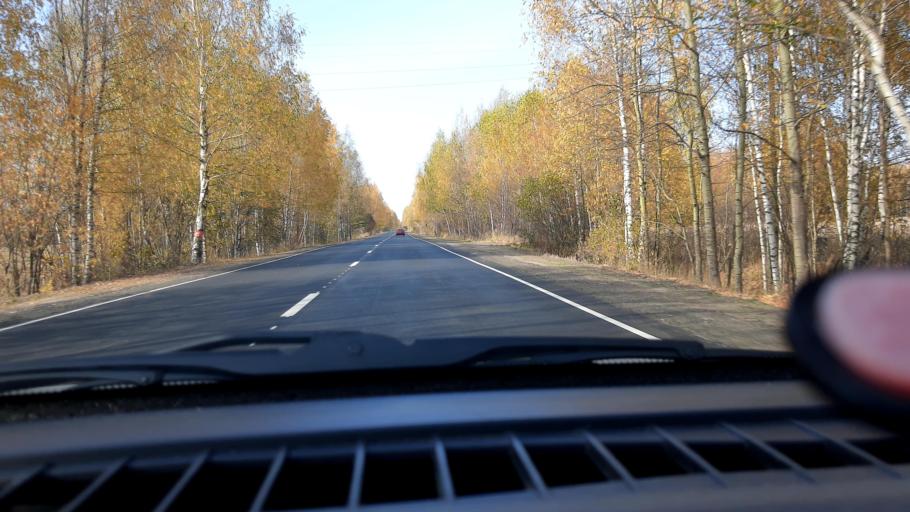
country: RU
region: Nizjnij Novgorod
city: Novaya Balakhna
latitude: 56.5550
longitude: 43.7409
